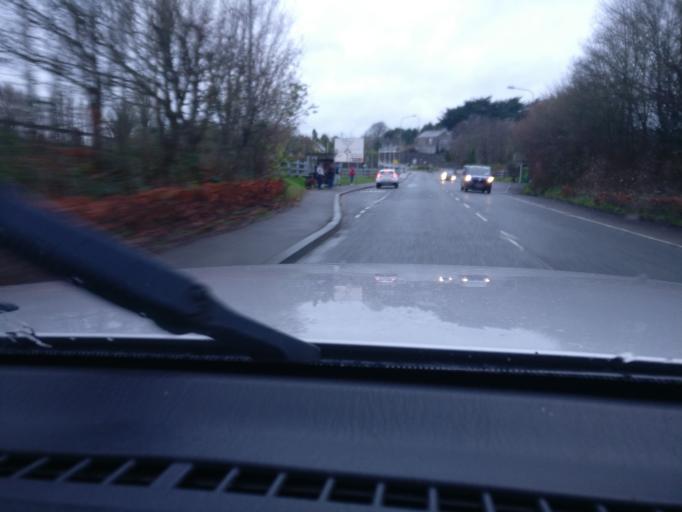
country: IE
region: Leinster
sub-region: An Mhi
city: Trim
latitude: 53.5535
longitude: -6.7849
